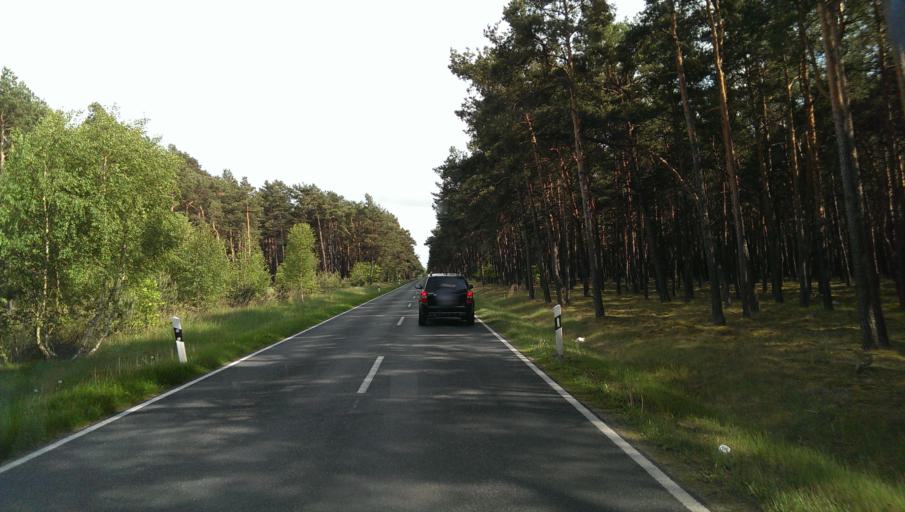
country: DE
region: Brandenburg
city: Bruck
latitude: 52.1744
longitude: 12.7605
